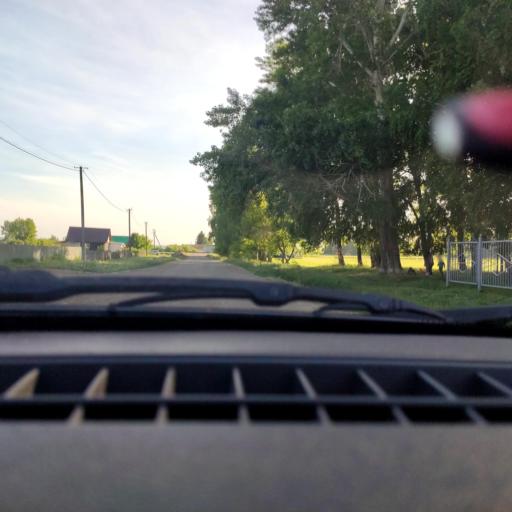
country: RU
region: Bashkortostan
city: Tolbazy
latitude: 54.2963
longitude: 55.8092
